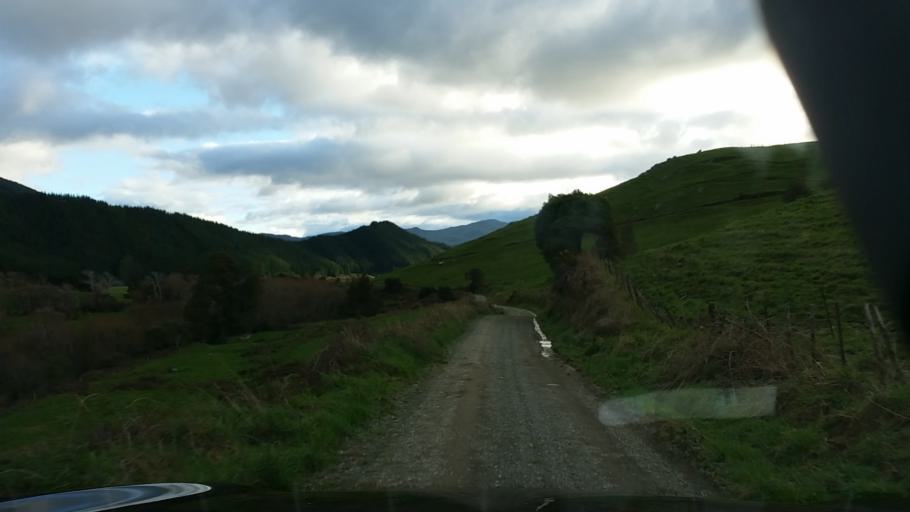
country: NZ
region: Nelson
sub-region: Nelson City
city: Nelson
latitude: -41.2083
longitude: 173.6362
